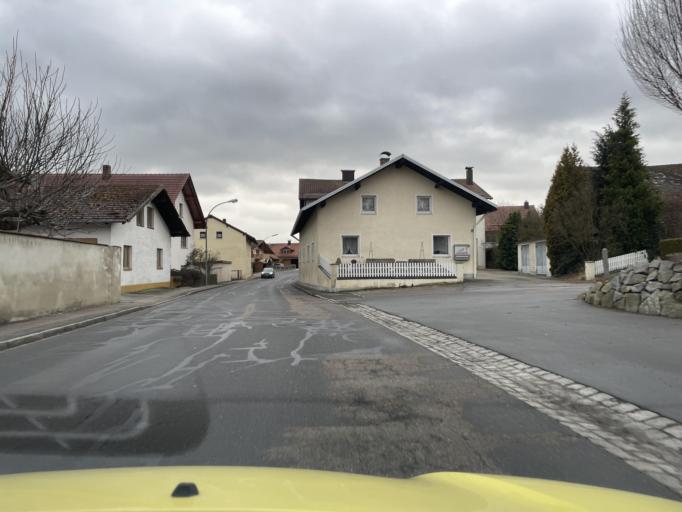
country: DE
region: Bavaria
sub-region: Upper Palatinate
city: Cham
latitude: 49.1932
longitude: 12.6712
